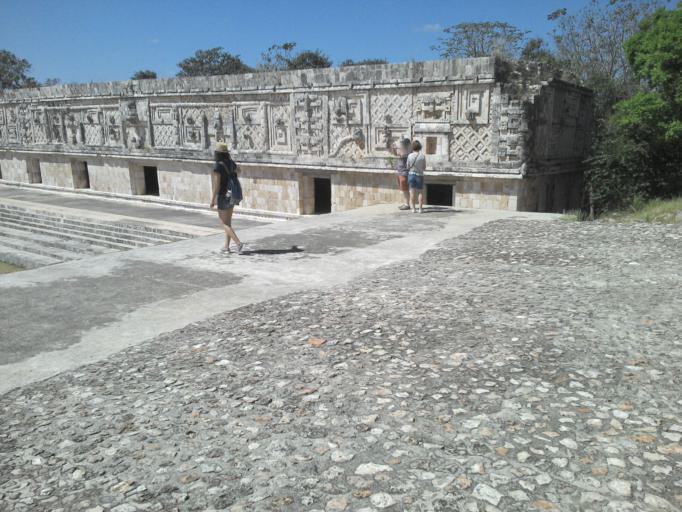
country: MX
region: Yucatan
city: Santa Elena
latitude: 20.3616
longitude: -89.7707
